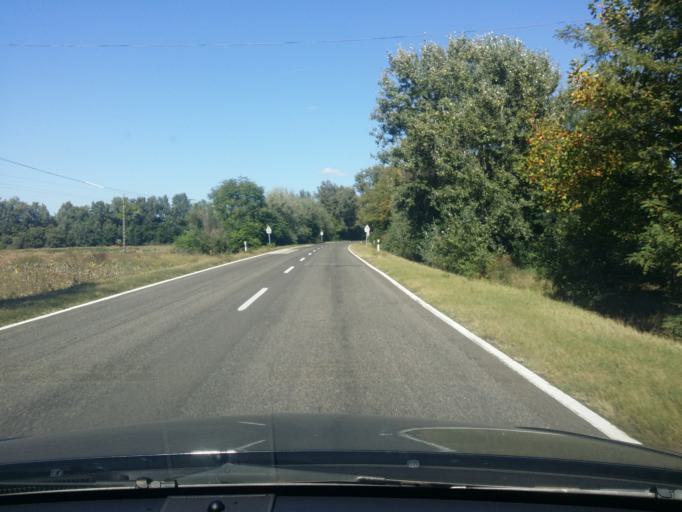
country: HU
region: Bacs-Kiskun
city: Palmonostora
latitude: 46.5920
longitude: 19.9227
